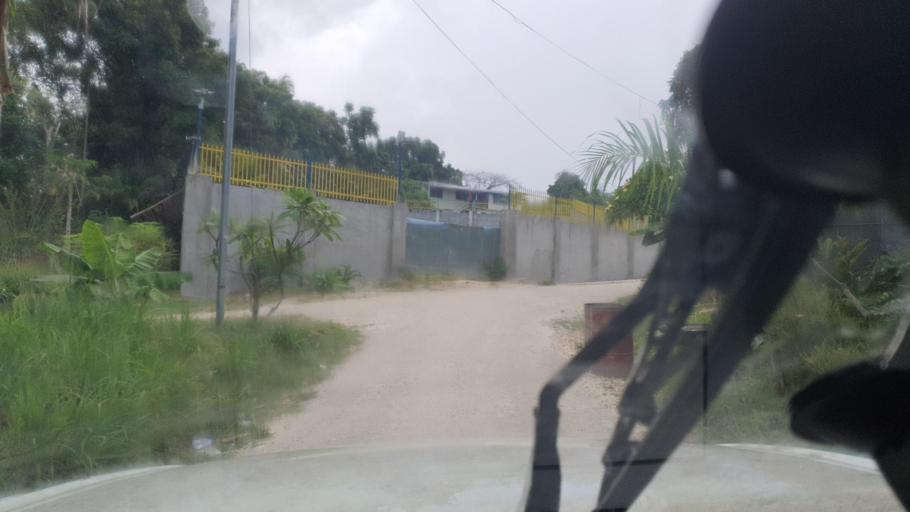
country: SB
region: Guadalcanal
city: Honiara
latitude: -9.4336
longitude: 159.9460
